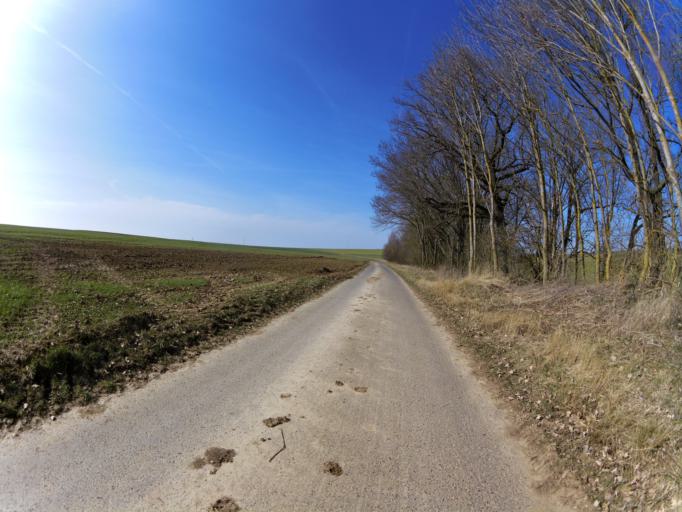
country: DE
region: Bavaria
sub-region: Regierungsbezirk Unterfranken
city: Dettelbach
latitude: 49.8251
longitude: 10.1412
